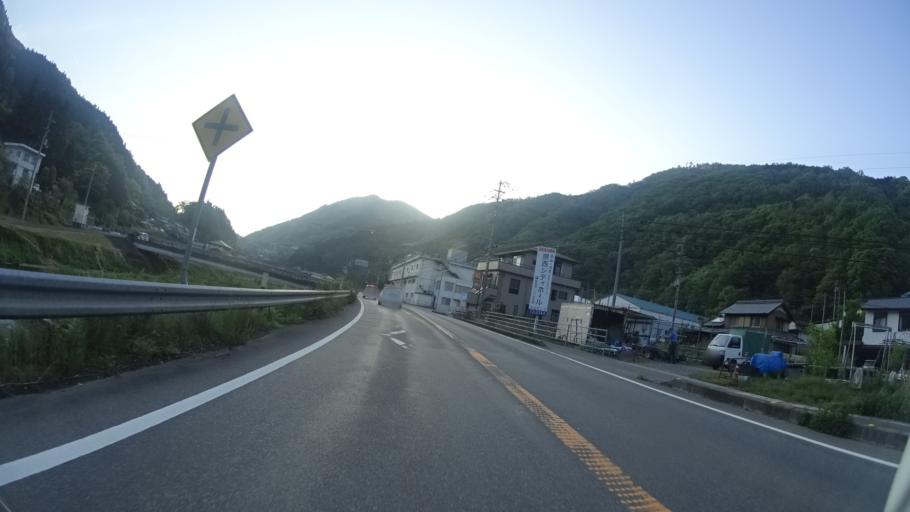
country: JP
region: Tokushima
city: Ikedacho
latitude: 34.0149
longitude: 133.7603
